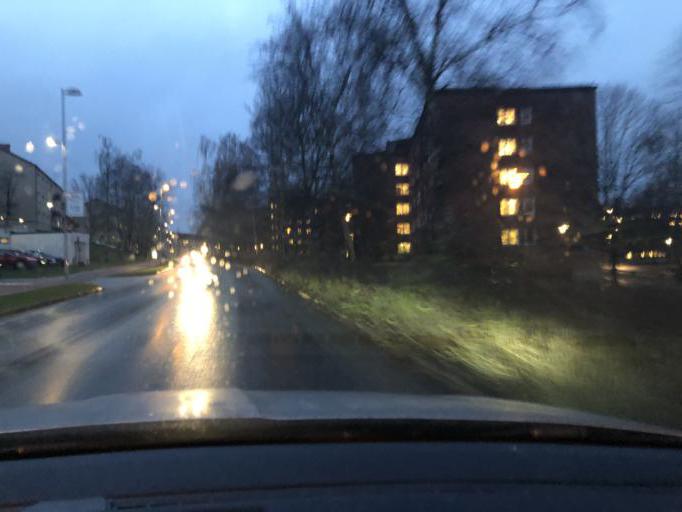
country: SE
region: Vaermland
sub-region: Karlstads Kommun
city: Karlstad
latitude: 59.3773
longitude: 13.4821
